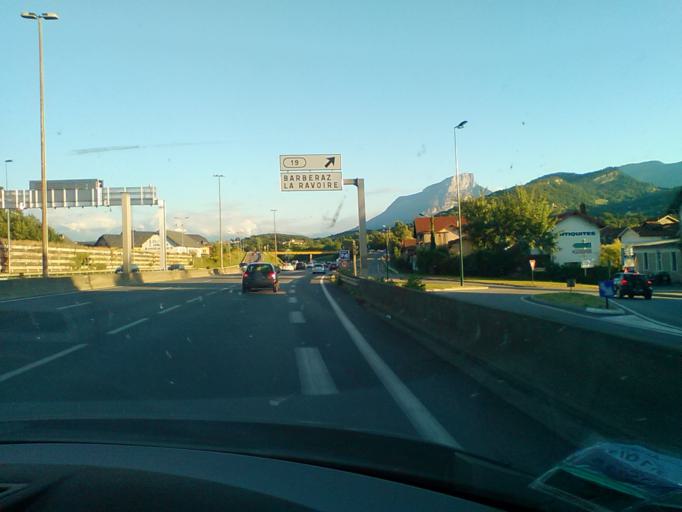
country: FR
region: Rhone-Alpes
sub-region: Departement de la Savoie
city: Chambery
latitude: 45.5627
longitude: 5.9483
